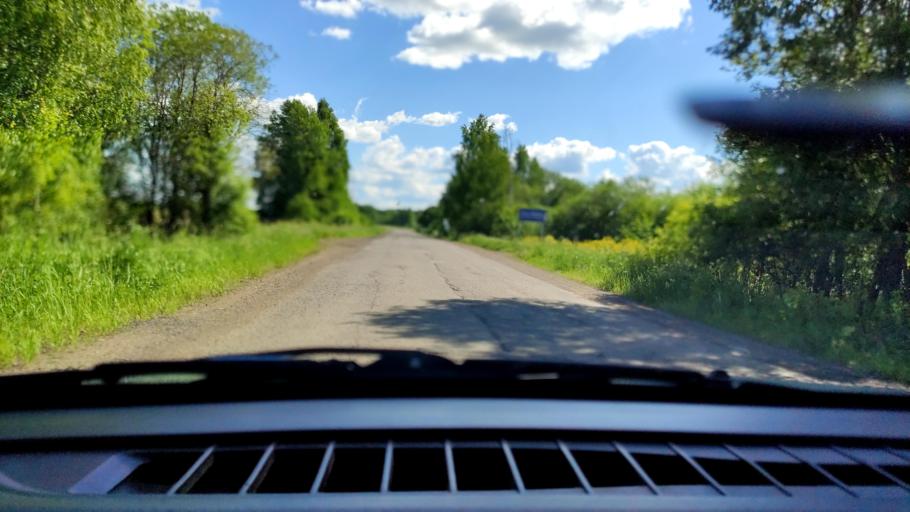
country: RU
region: Perm
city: Uinskoye
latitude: 57.2418
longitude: 56.5315
